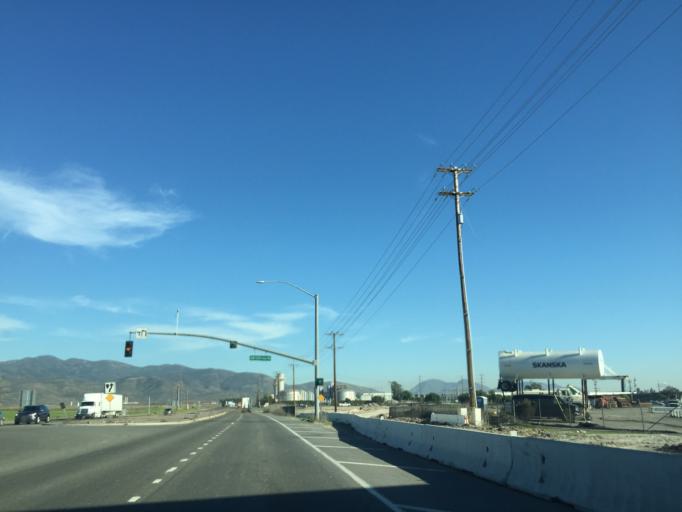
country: MX
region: Baja California
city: Tijuana
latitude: 32.5675
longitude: -116.9484
